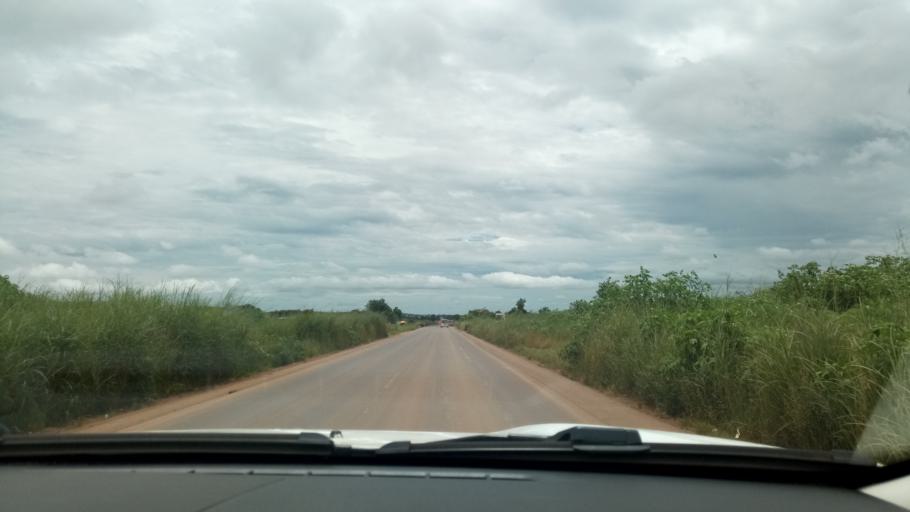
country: CD
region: Katanga
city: Lubumbashi
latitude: -11.5722
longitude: 27.5427
